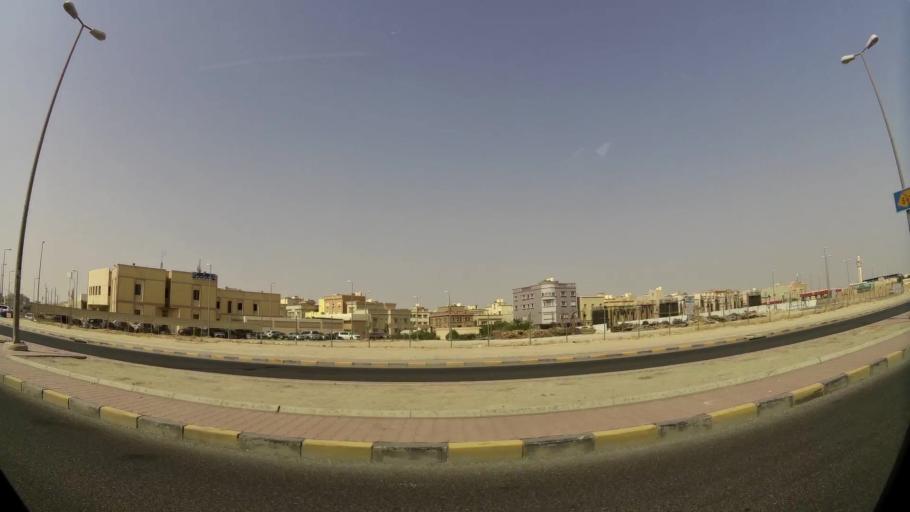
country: KW
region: Muhafazat al Jahra'
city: Al Jahra'
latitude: 29.3067
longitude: 47.6997
